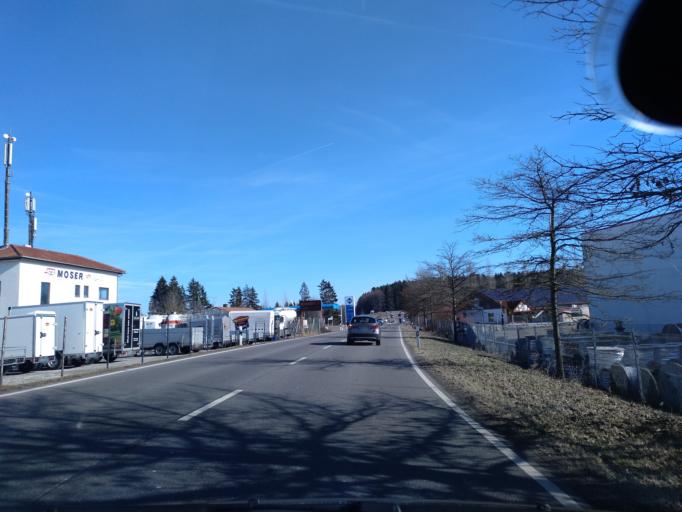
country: DE
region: Baden-Wuerttemberg
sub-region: Regierungsbezirk Stuttgart
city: Mainhardt
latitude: 49.0769
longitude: 9.5616
